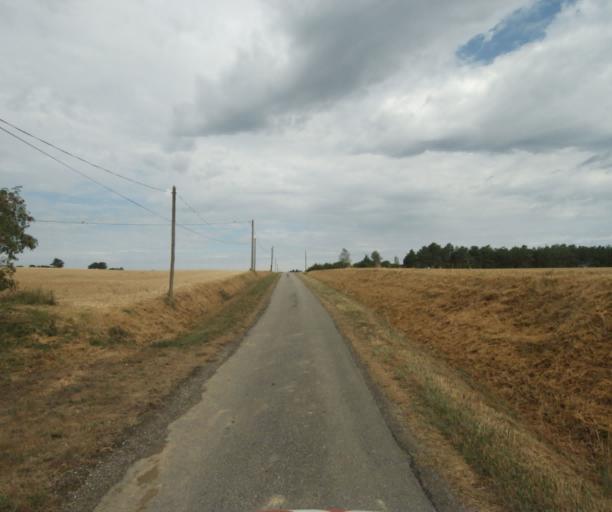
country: FR
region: Midi-Pyrenees
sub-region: Departement de la Haute-Garonne
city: Revel
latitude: 43.4396
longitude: 1.9609
